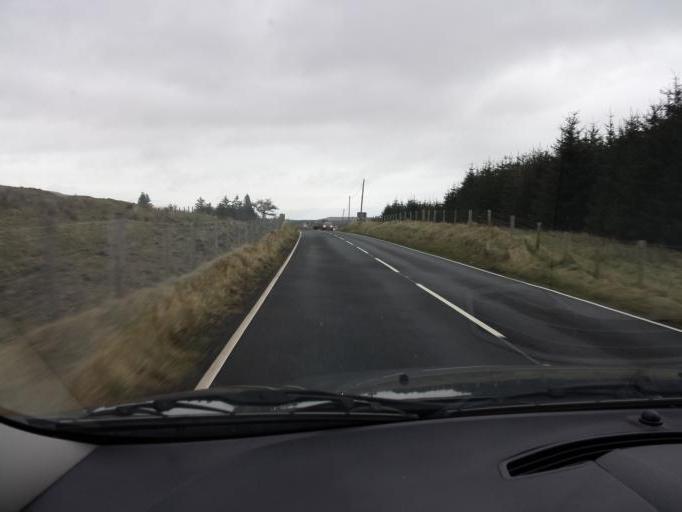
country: GB
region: Northern Ireland
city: Glenariff
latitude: 55.0117
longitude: -6.1479
